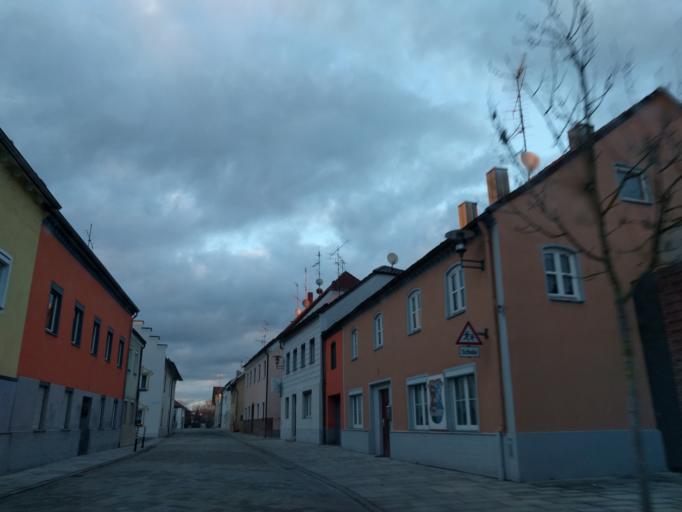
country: DE
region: Bavaria
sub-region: Lower Bavaria
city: Hofkirchen
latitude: 48.6782
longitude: 13.1182
